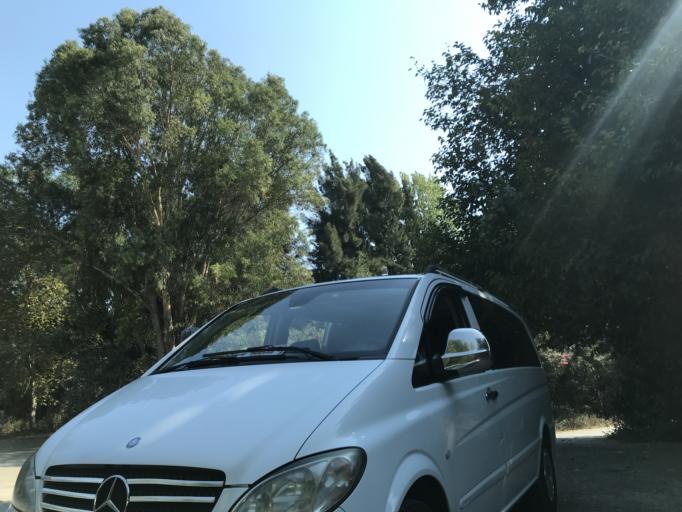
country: TR
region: Izmir
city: Selcuk
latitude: 37.9492
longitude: 27.3632
